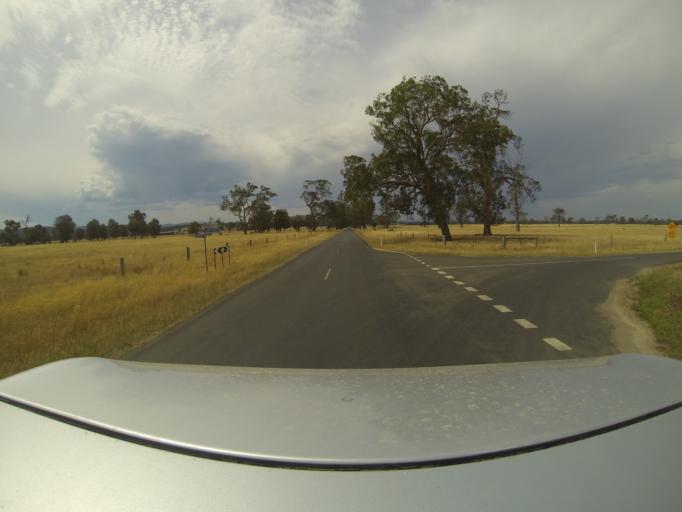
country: AU
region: Victoria
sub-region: Wellington
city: Heyfield
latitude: -37.9802
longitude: 146.6948
